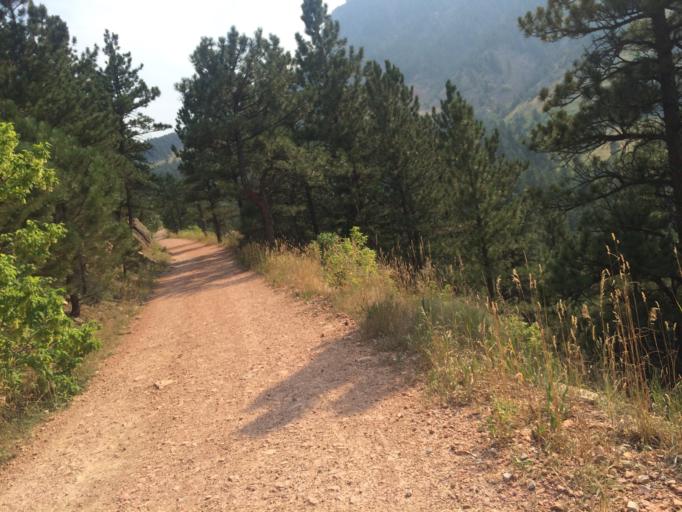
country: US
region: Colorado
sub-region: Boulder County
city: Boulder
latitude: 39.9306
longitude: -105.2755
